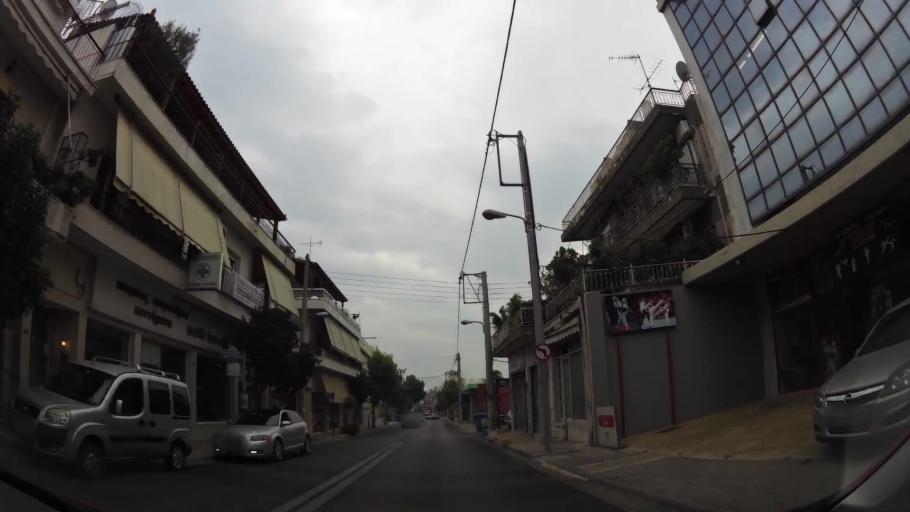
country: GR
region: Attica
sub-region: Nomarchia Athinas
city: Ilion
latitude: 38.0206
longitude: 23.7098
